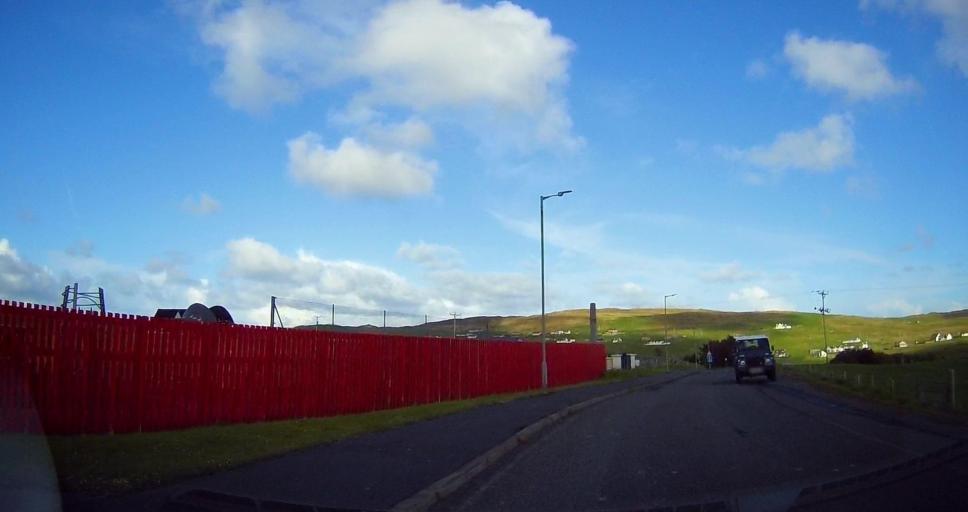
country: GB
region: Scotland
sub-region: Shetland Islands
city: Shetland
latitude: 60.3691
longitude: -1.1399
